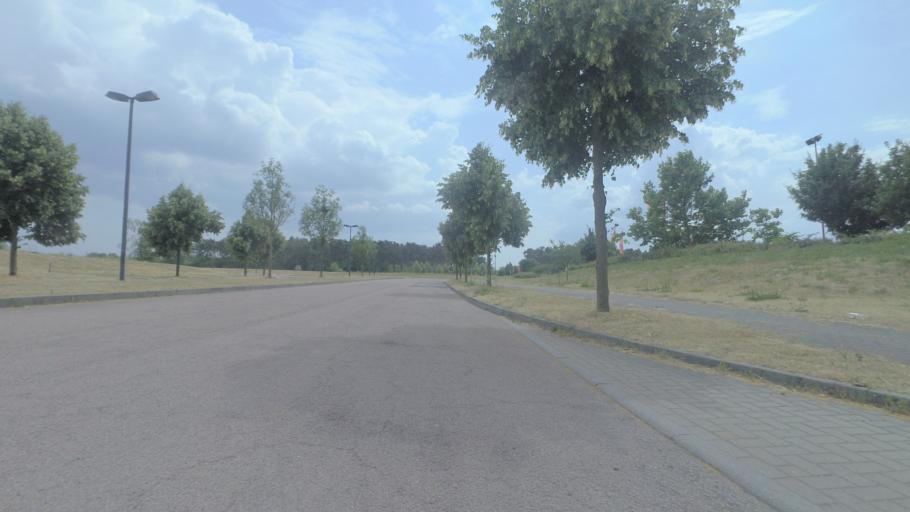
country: DE
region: Brandenburg
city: Grossbeeren
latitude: 52.3207
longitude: 13.2926
